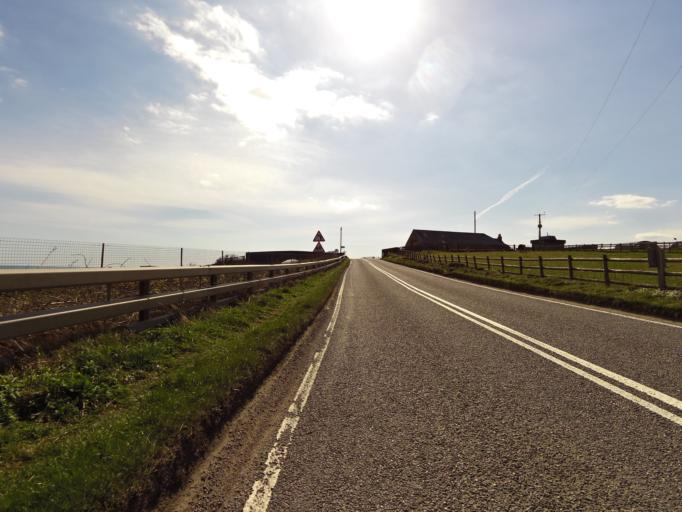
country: GB
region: Scotland
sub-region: Aberdeen City
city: Aberdeen
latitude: 57.1223
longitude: -2.0573
